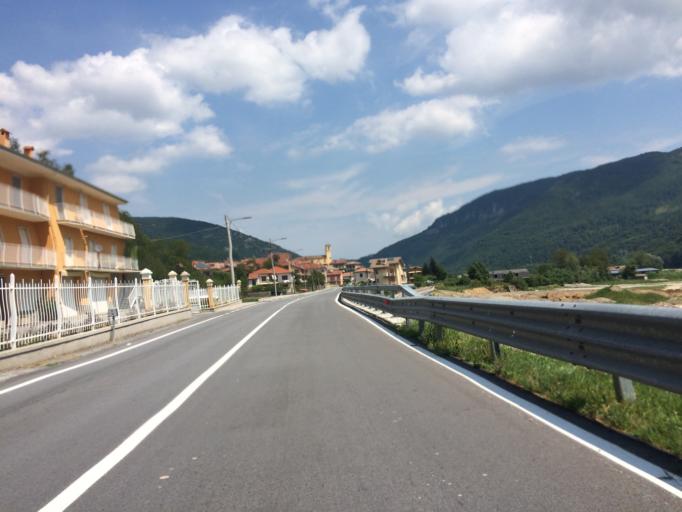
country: IT
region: Piedmont
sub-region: Provincia di Cuneo
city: Priola
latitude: 44.2557
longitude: 8.0202
